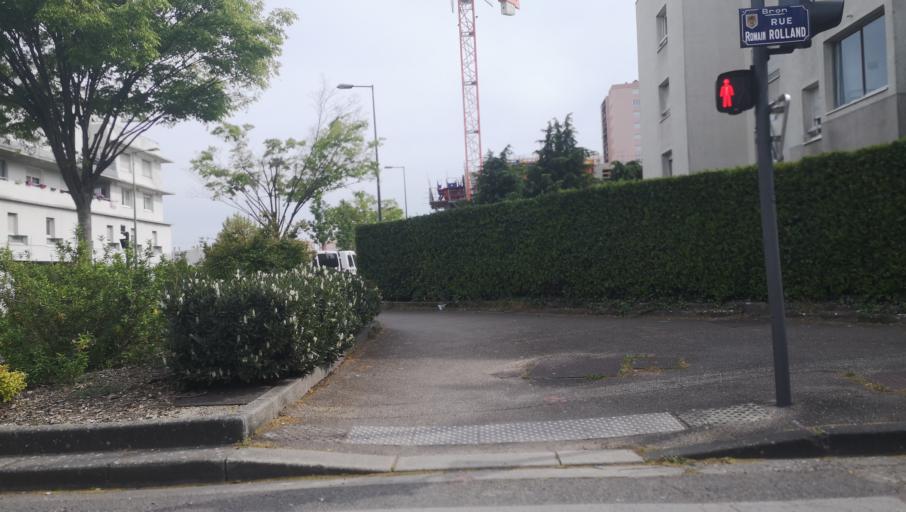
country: FR
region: Rhone-Alpes
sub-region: Departement du Rhone
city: Bron
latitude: 45.7451
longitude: 4.9186
